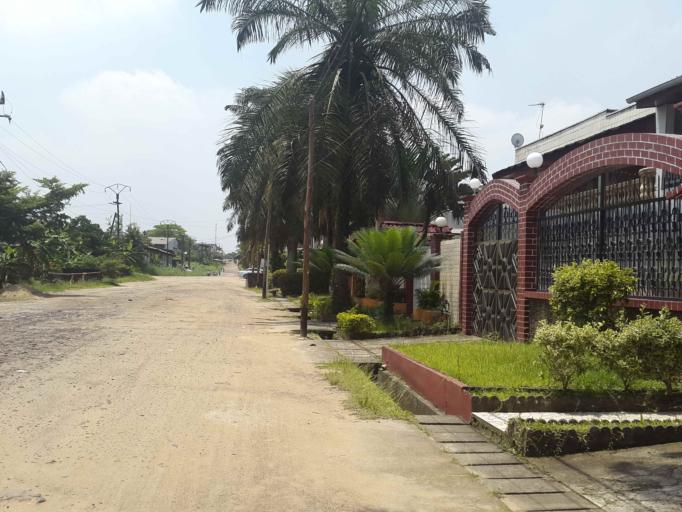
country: CM
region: Littoral
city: Douala
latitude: 4.0939
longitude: 9.7312
